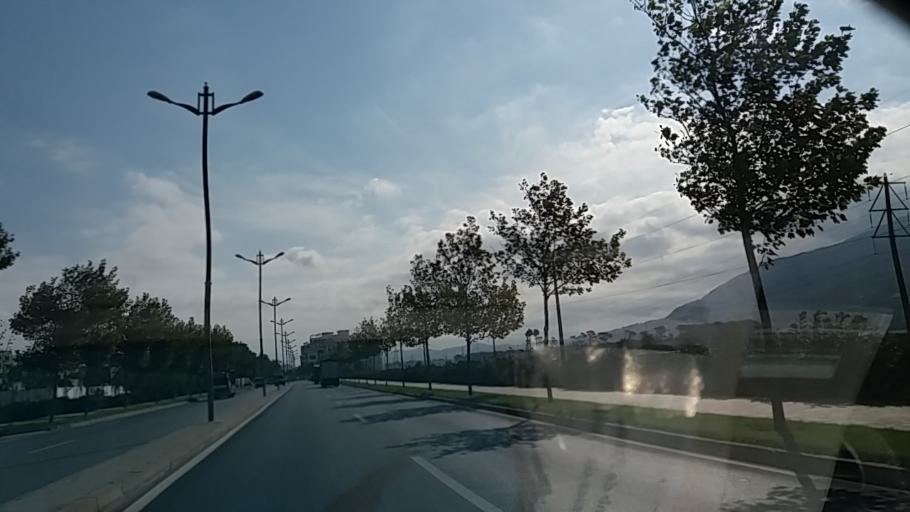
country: MA
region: Tanger-Tetouan
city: Tetouan
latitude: 35.5651
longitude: -5.4178
